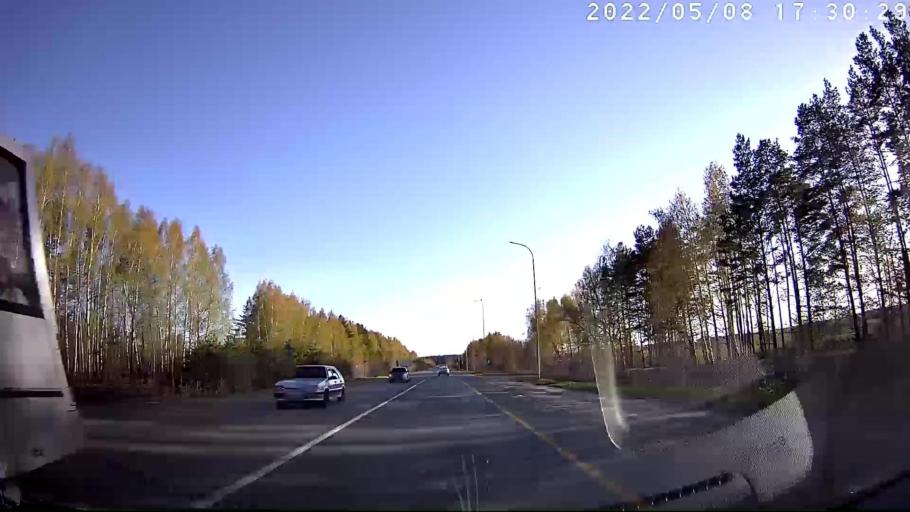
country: RU
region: Mariy-El
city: Volzhsk
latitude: 55.9096
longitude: 48.3626
